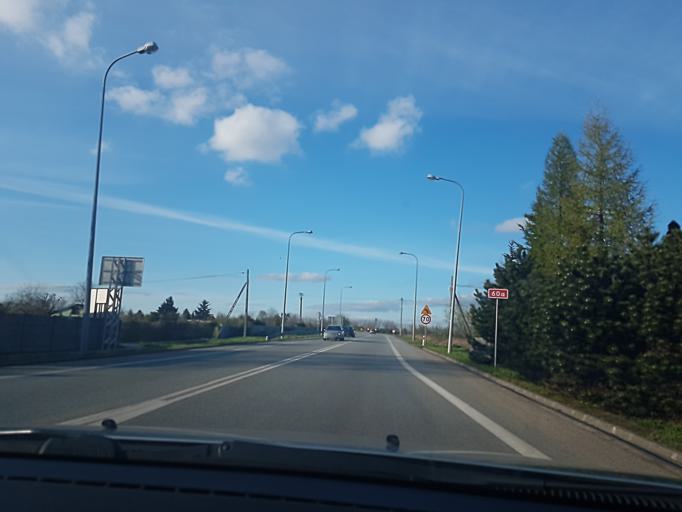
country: PL
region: Lodz Voivodeship
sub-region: Powiat kutnowski
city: Kutno
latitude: 52.2276
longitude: 19.3869
